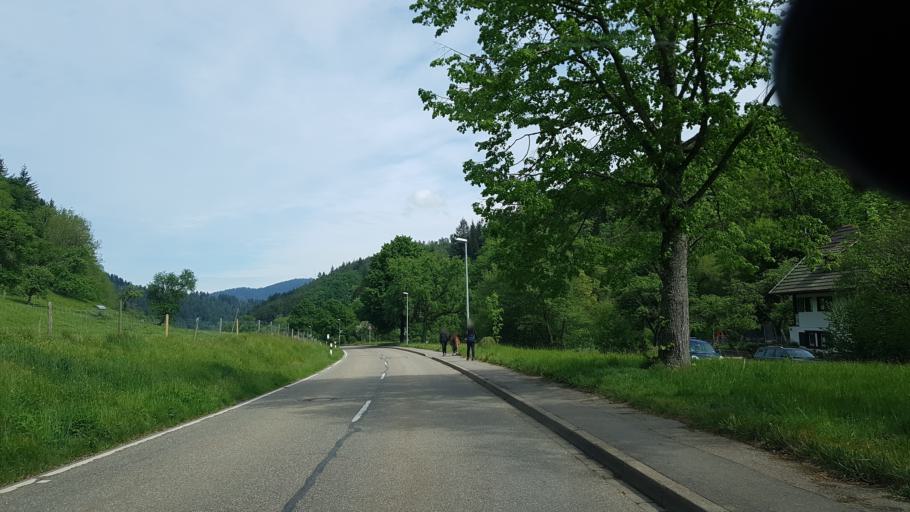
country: DE
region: Baden-Wuerttemberg
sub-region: Freiburg Region
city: Kirchzarten
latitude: 47.9543
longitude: 7.9131
